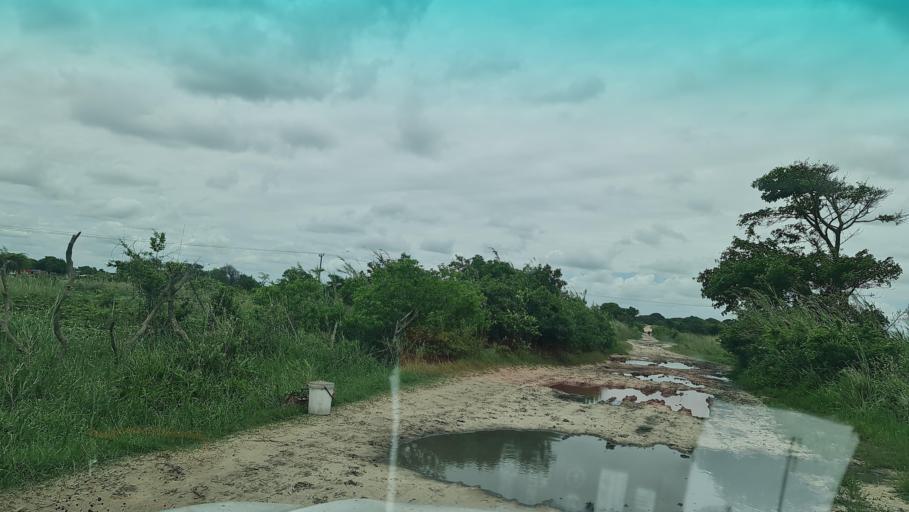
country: MZ
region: Maputo City
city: Maputo
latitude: -25.7018
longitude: 32.7046
